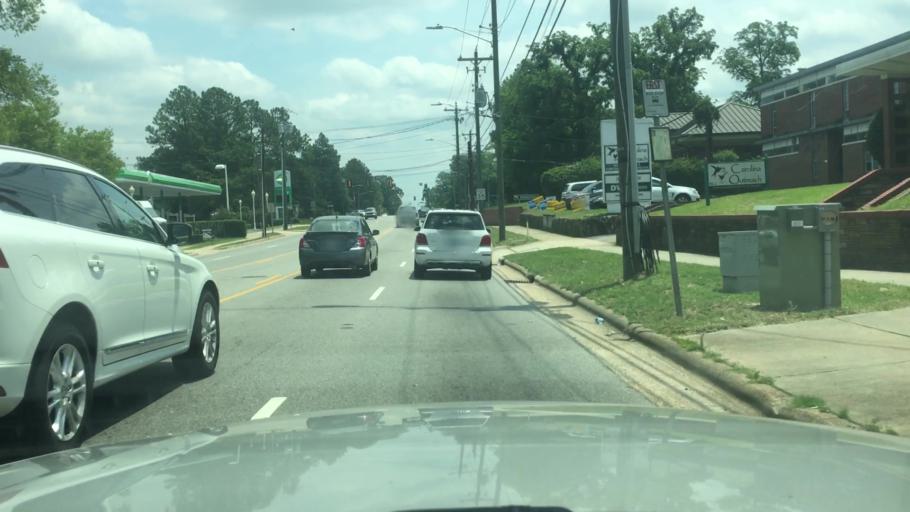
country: US
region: North Carolina
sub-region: Cumberland County
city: Fayetteville
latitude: 35.0562
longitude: -78.8961
